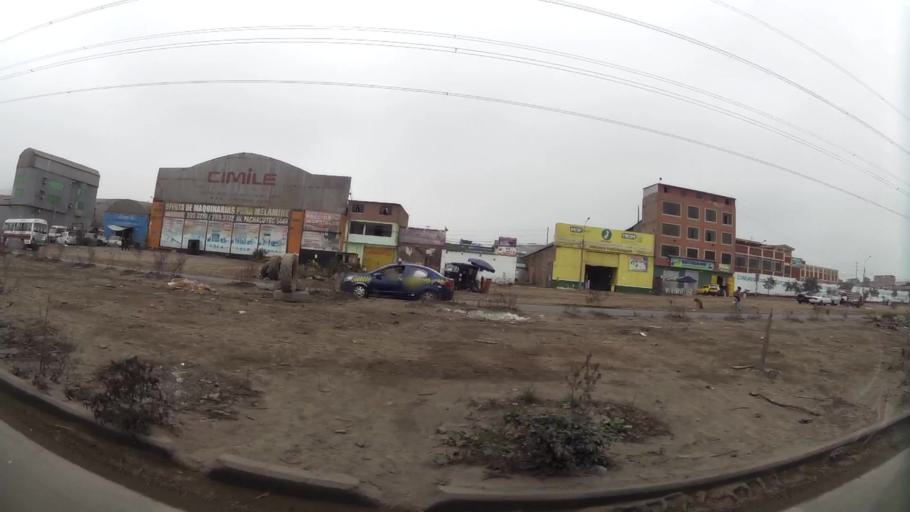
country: PE
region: Lima
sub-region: Lima
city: Surco
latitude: -12.1972
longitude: -76.9337
